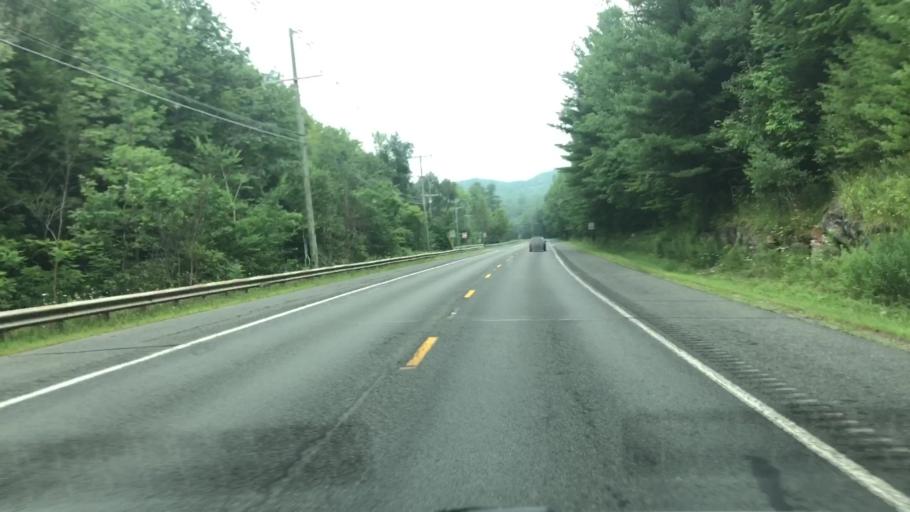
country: US
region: Massachusetts
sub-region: Berkshire County
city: Lanesborough
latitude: 42.5521
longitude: -73.2351
